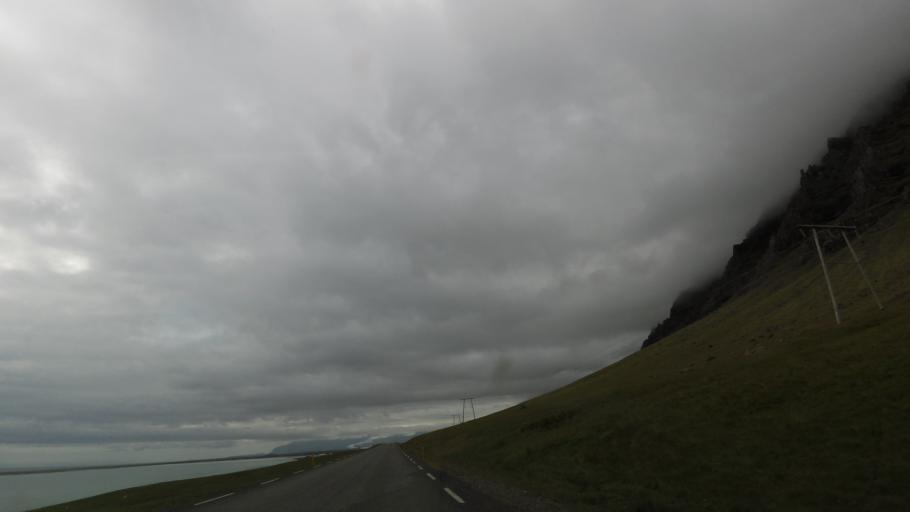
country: IS
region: East
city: Hoefn
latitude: 64.1358
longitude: -15.9848
